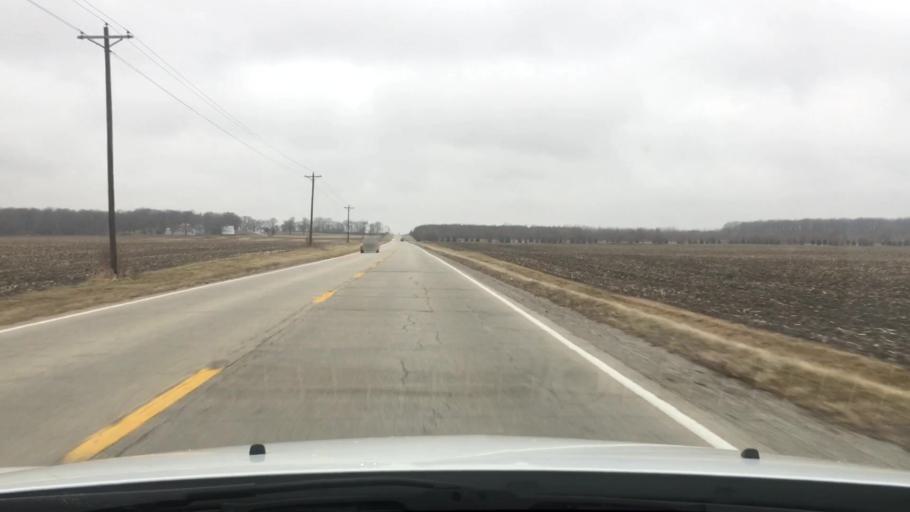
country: US
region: Illinois
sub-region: Iroquois County
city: Watseka
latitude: 40.8912
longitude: -87.6755
